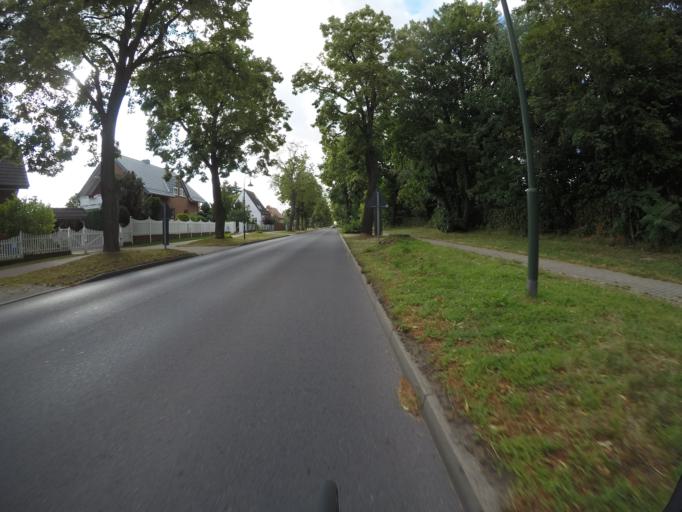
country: DE
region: Brandenburg
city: Ahrensfelde
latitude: 52.5808
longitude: 13.5698
